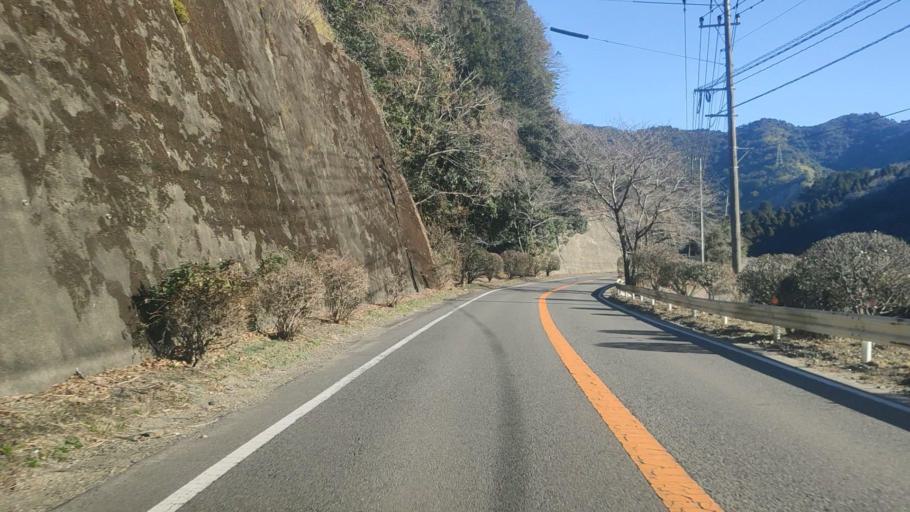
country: JP
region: Miyazaki
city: Nobeoka
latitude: 32.6231
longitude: 131.7091
